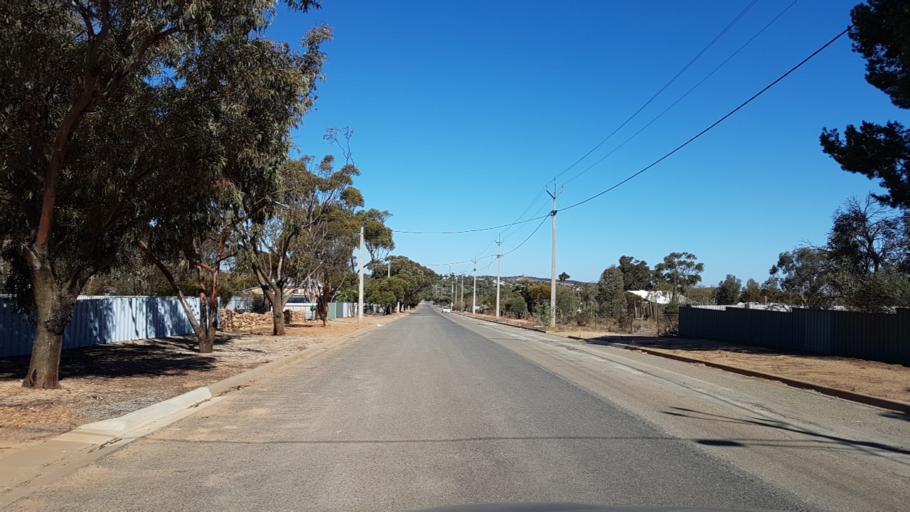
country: AU
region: South Australia
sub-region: Peterborough
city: Peterborough
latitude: -32.9660
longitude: 138.8317
